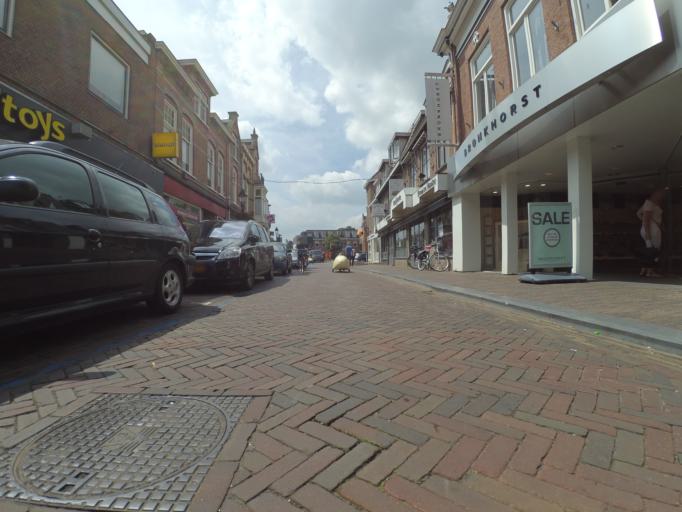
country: NL
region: South Holland
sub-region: Gemeente Leerdam
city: Leerdam
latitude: 51.8911
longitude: 5.0940
